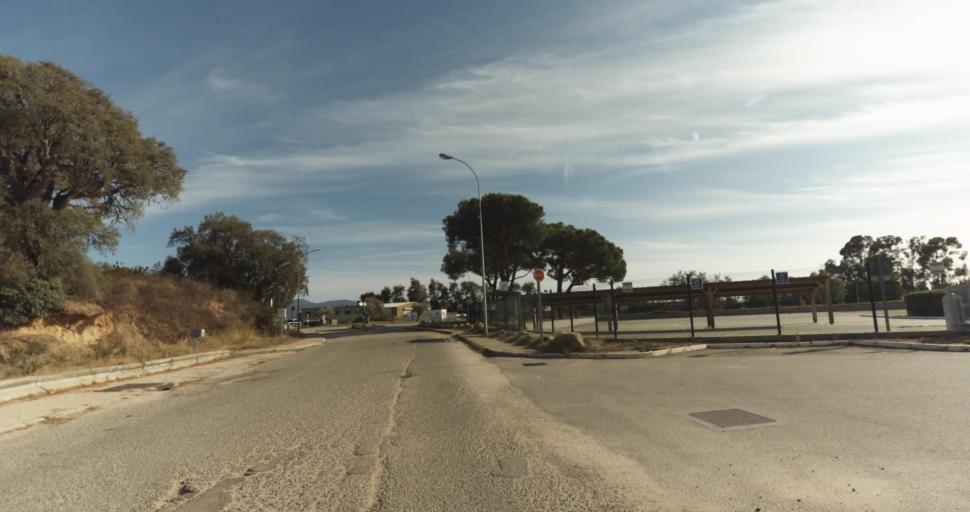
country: FR
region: Corsica
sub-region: Departement de la Corse-du-Sud
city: Ajaccio
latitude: 41.9308
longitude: 8.7872
